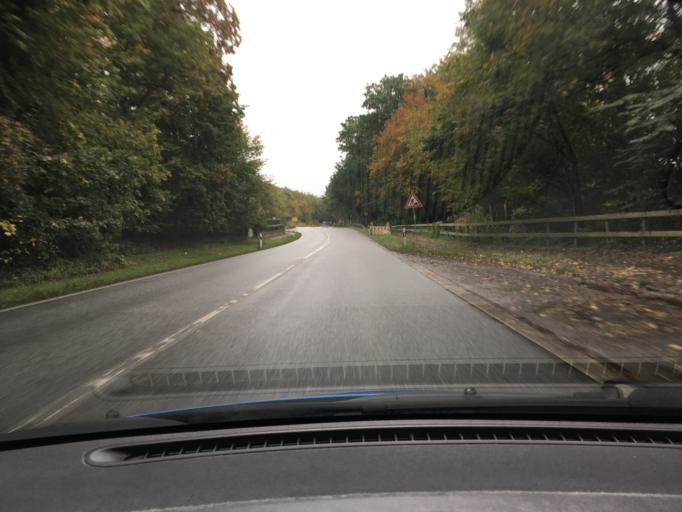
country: DE
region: Schleswig-Holstein
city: Bosdorf
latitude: 54.1413
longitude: 10.4741
